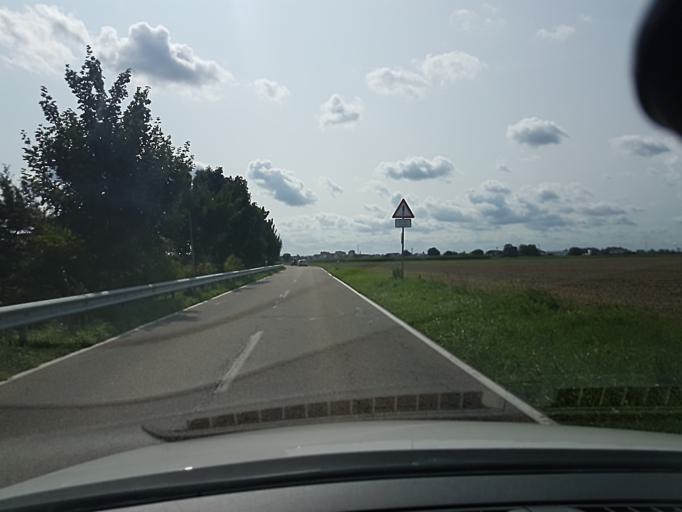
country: DE
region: Rheinland-Pfalz
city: Otterstadt
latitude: 49.3799
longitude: 8.4402
